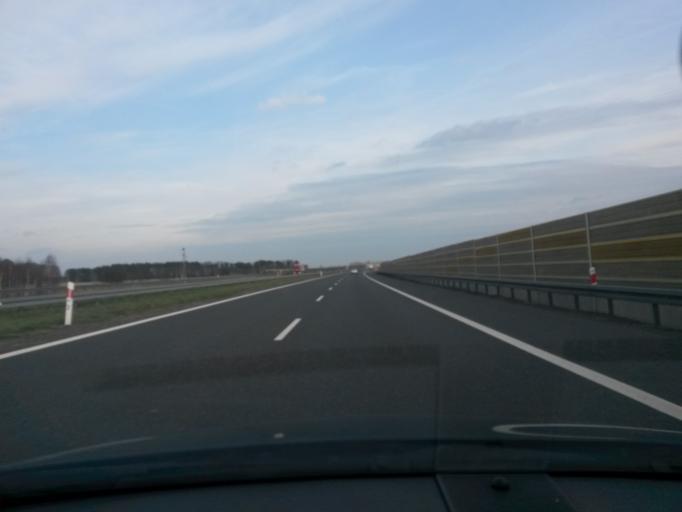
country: PL
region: Lodz Voivodeship
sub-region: Powiat zgierski
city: Parzeczew
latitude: 51.9521
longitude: 19.1538
